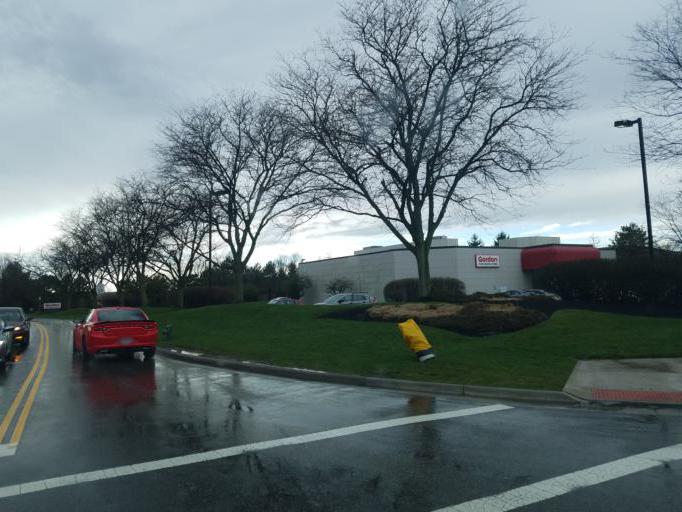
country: US
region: Ohio
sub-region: Franklin County
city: Dublin
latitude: 40.0986
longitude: -83.0948
